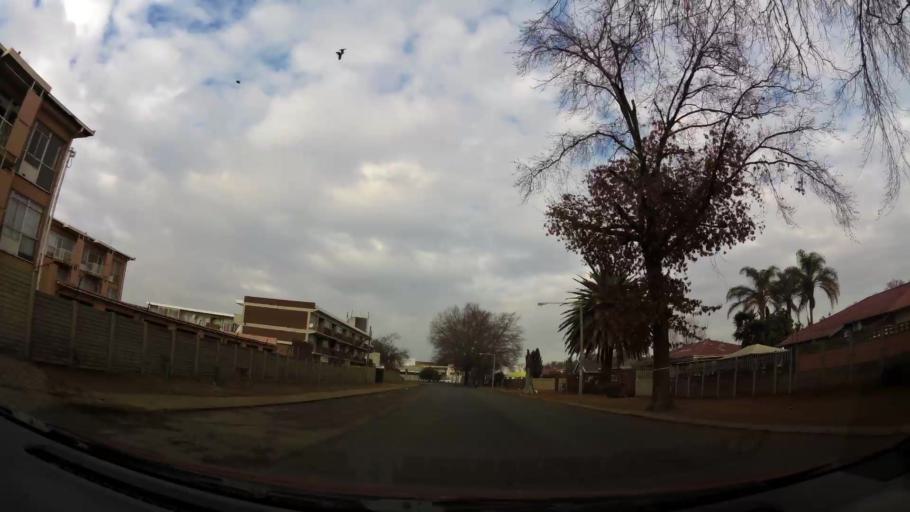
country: ZA
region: Gauteng
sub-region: Sedibeng District Municipality
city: Vanderbijlpark
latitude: -26.6931
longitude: 27.8261
